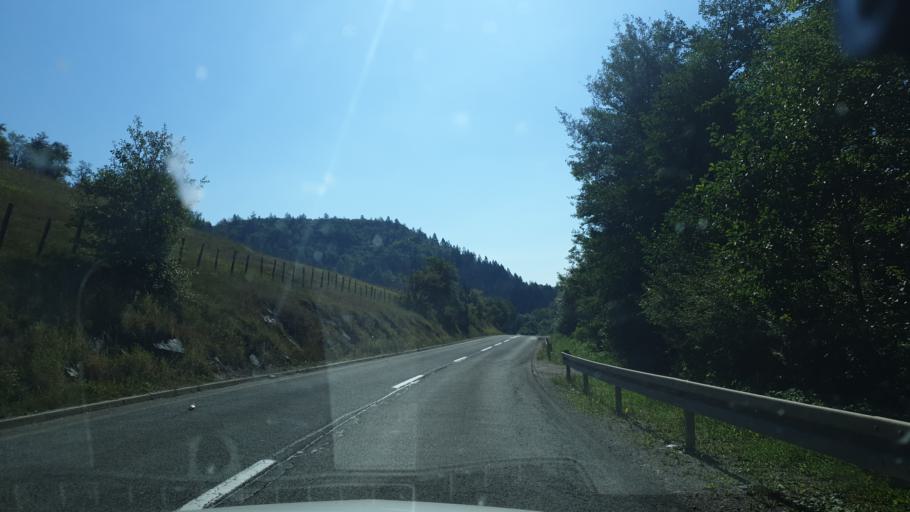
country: RS
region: Central Serbia
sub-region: Zlatiborski Okrug
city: Nova Varos
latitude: 43.5515
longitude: 19.7776
